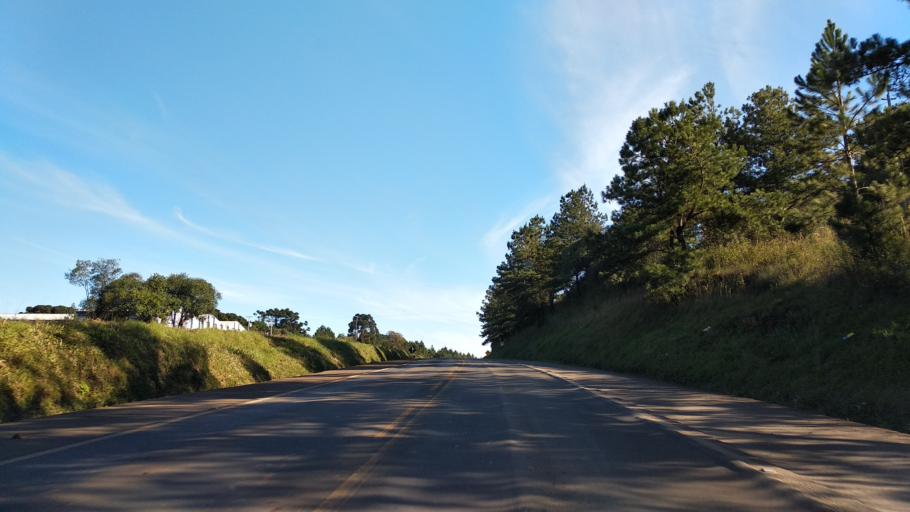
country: BR
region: Santa Catarina
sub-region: Campos Novos
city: Campos Novos
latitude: -27.4054
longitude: -51.2068
